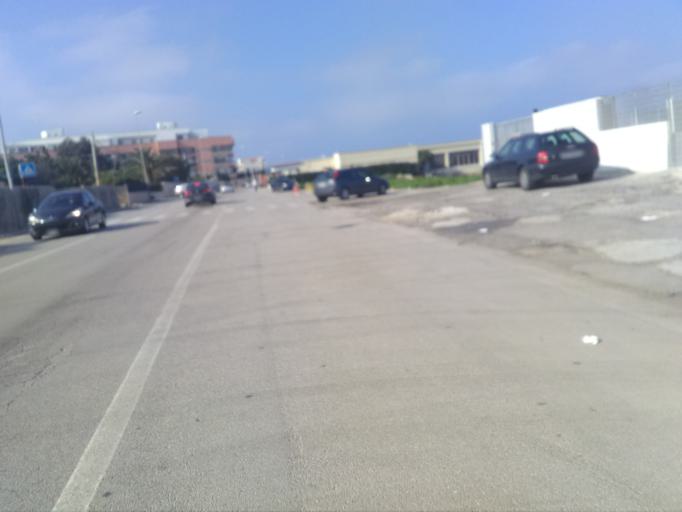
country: IT
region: Apulia
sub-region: Provincia di Bari
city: San Paolo
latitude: 41.1633
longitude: 16.7587
